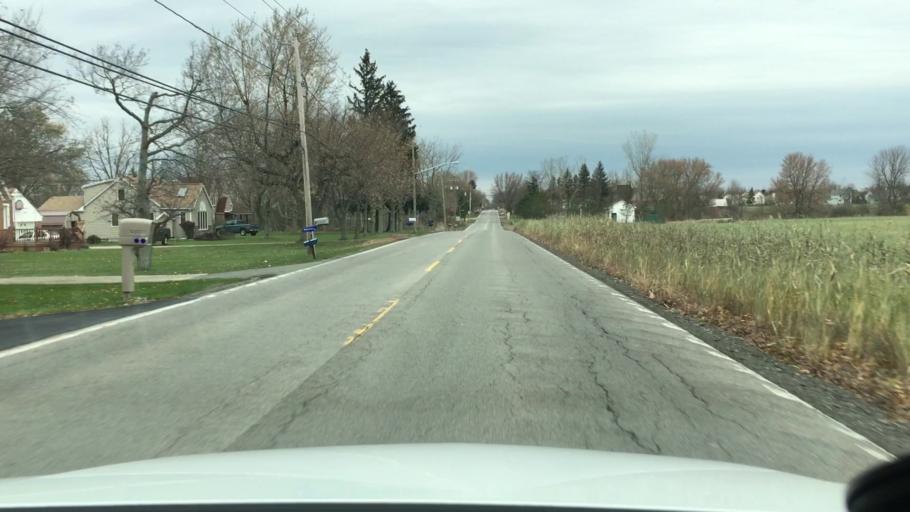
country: US
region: New York
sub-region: Erie County
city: Lancaster
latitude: 42.8617
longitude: -78.6761
